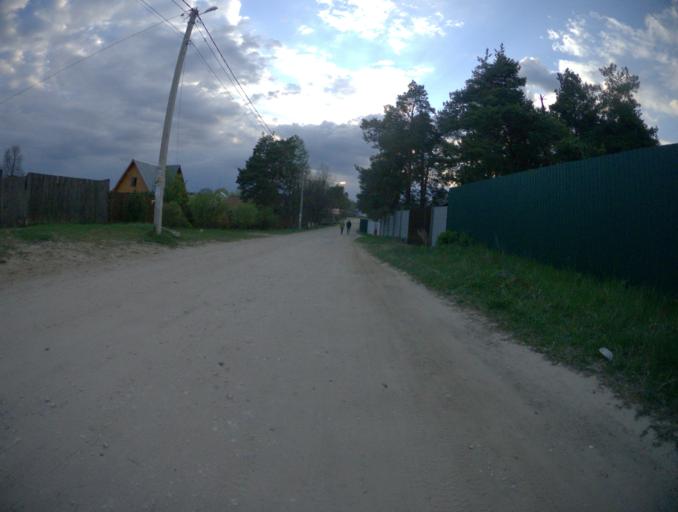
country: RU
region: Vladimir
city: Raduzhnyy
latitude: 56.0281
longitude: 40.3898
